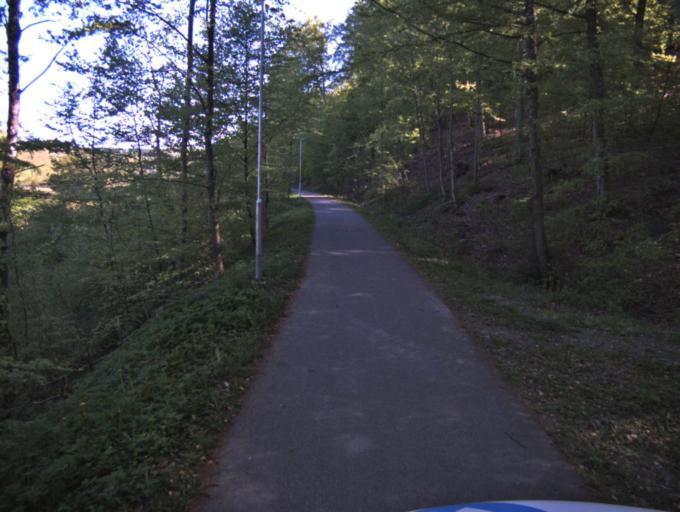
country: SE
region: Skane
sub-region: Kristianstads Kommun
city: Degeberga
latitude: 55.8352
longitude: 14.0786
